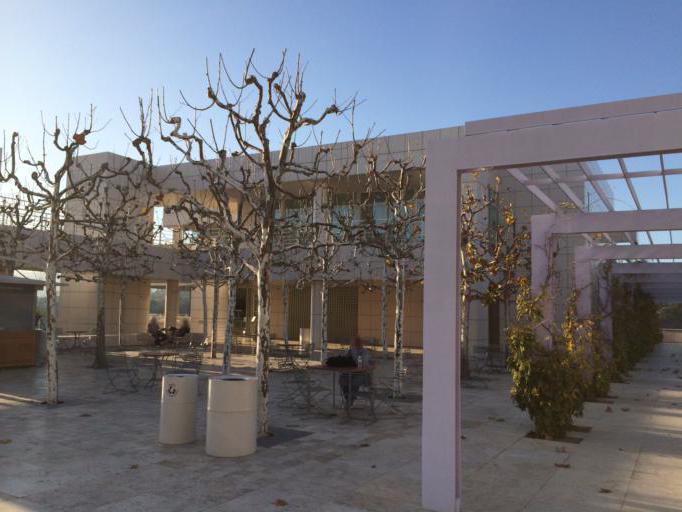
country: US
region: California
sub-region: Los Angeles County
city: Westwood, Los Angeles
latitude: 34.0777
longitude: -118.4750
